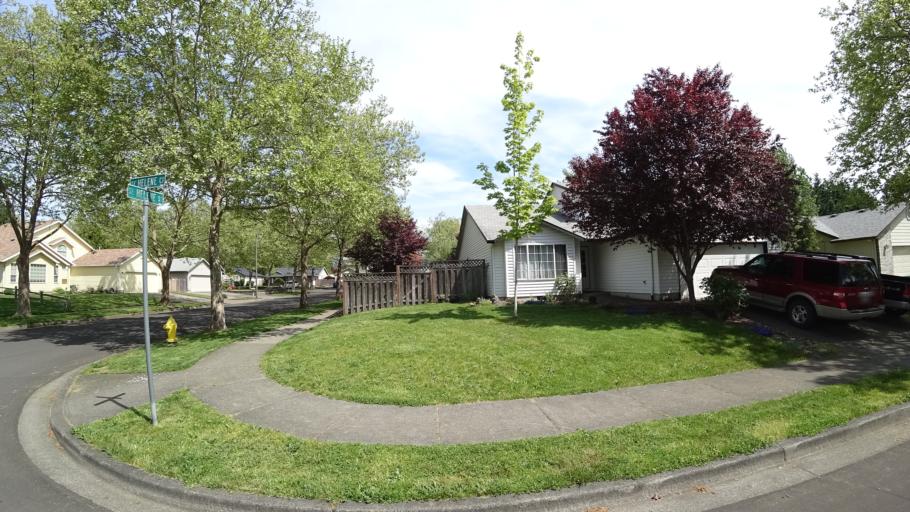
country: US
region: Oregon
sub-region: Washington County
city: Aloha
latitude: 45.5118
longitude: -122.9242
